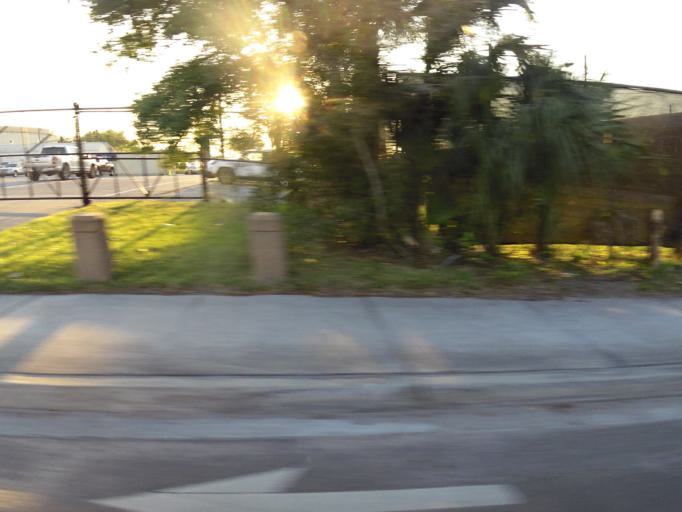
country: US
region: Florida
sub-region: Duval County
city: Jacksonville
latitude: 30.3284
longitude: -81.7056
